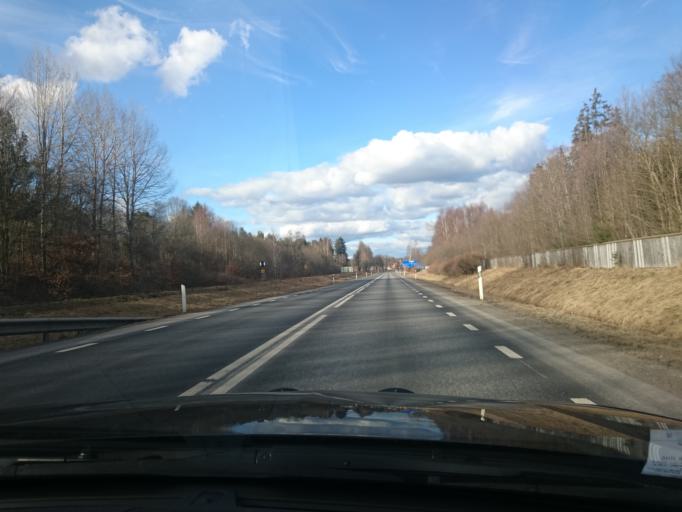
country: SE
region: Joenkoeping
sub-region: Vetlanda Kommun
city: Vetlanda
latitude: 57.4101
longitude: 15.0908
